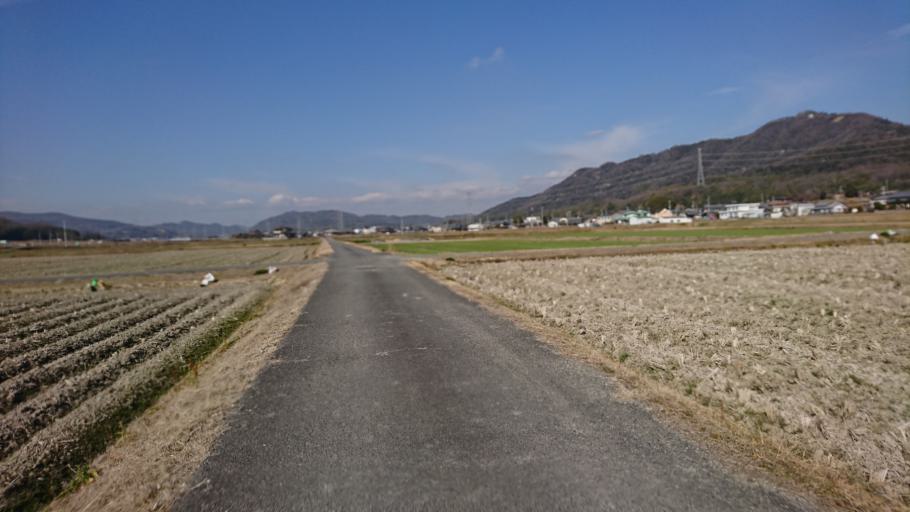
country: JP
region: Hyogo
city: Kakogawacho-honmachi
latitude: 34.8169
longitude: 134.8525
